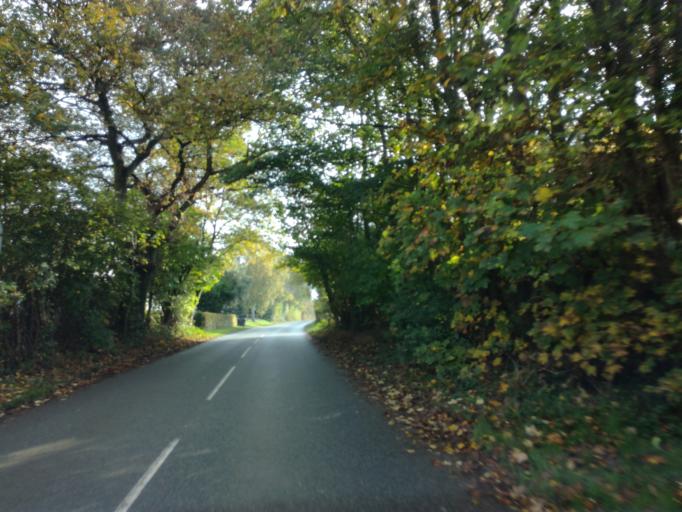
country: DK
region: South Denmark
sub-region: Vejle Kommune
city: Borkop
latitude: 55.6523
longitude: 9.6521
